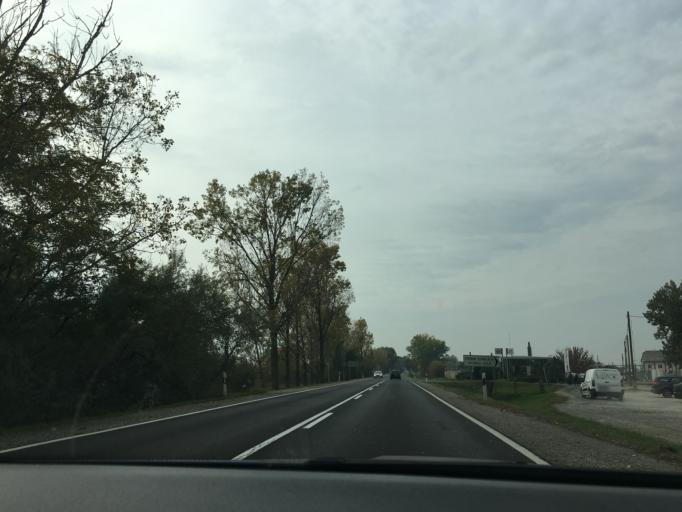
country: HU
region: Hajdu-Bihar
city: Debrecen
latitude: 47.5038
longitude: 21.5887
